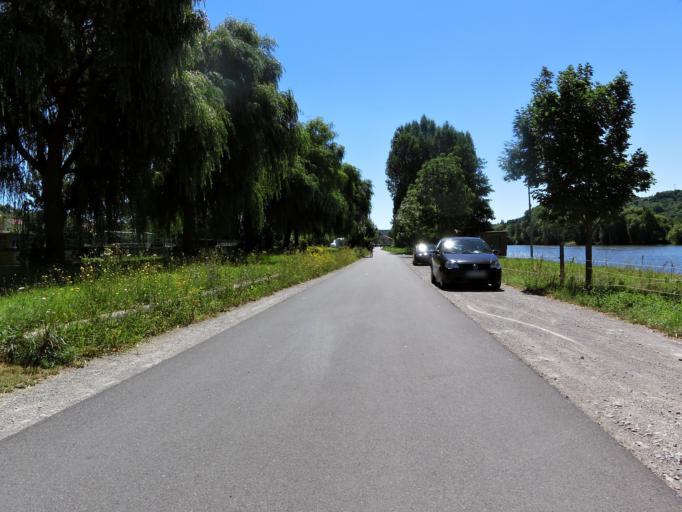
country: DE
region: Bavaria
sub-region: Regierungsbezirk Unterfranken
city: Ochsenfurt
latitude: 49.6746
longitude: 10.0447
